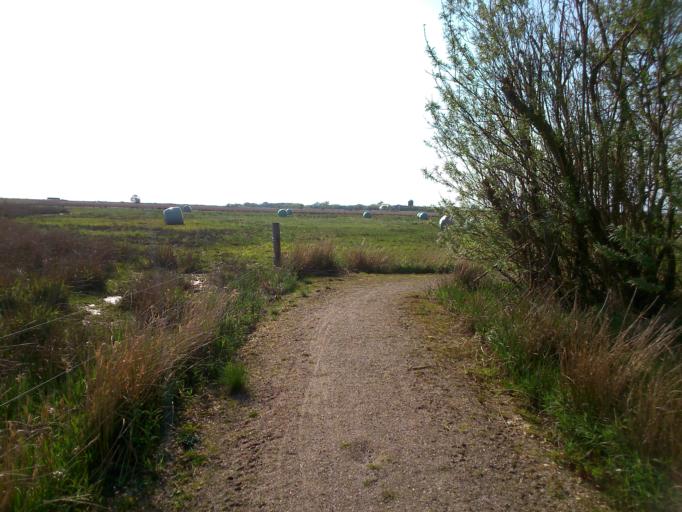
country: DK
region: Central Jutland
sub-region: Ringkobing-Skjern Kommune
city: Skjern
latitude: 55.9303
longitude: 8.4773
